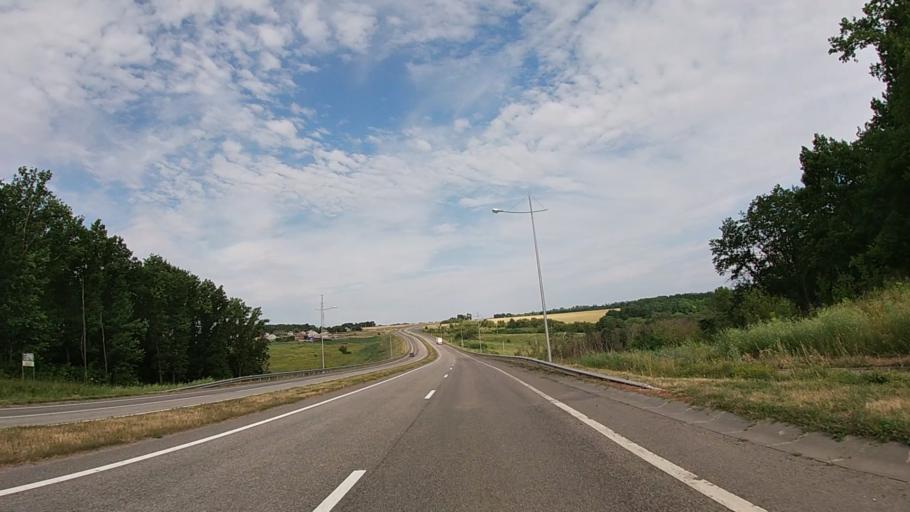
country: RU
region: Belgorod
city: Tomarovka
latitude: 50.7070
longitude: 36.2070
